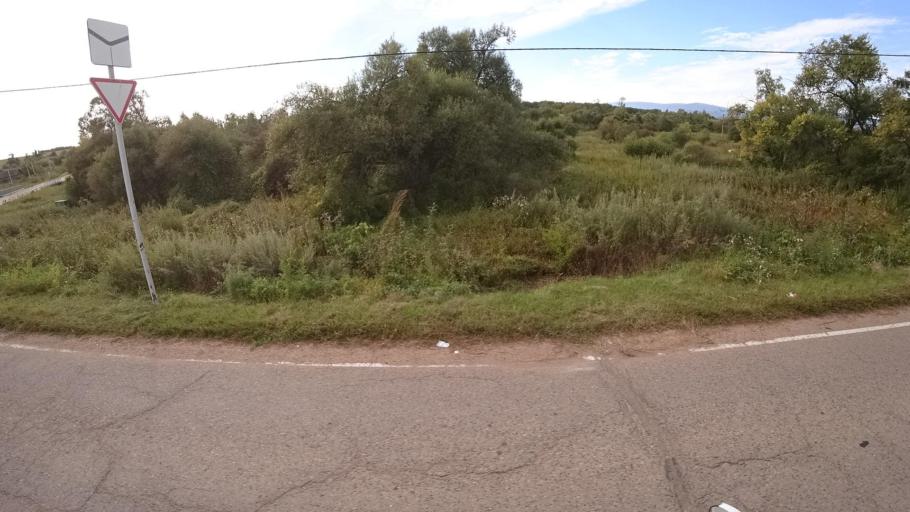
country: RU
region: Primorskiy
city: Dostoyevka
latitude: 44.3214
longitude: 133.4760
